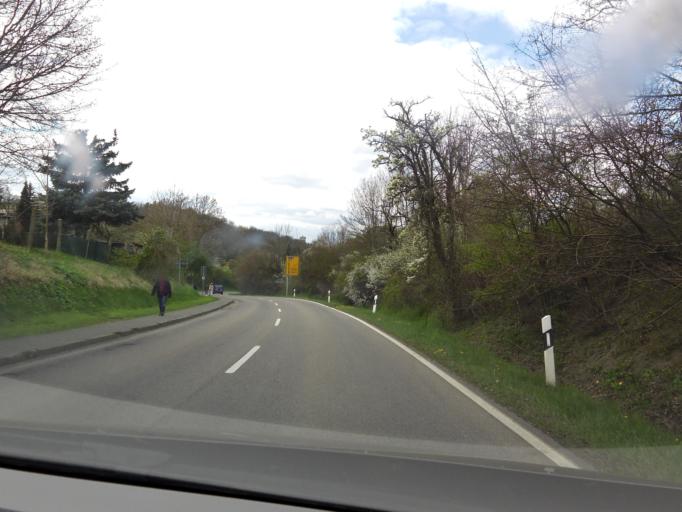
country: DE
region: Saxony-Anhalt
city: Eckartsberga
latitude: 51.1202
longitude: 11.5680
